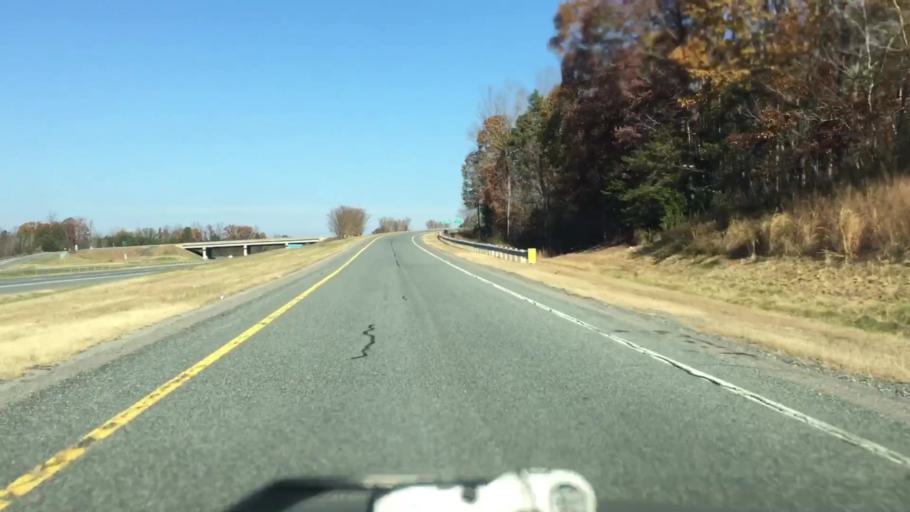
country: US
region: North Carolina
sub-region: Rockingham County
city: Reidsville
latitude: 36.3081
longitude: -79.6433
